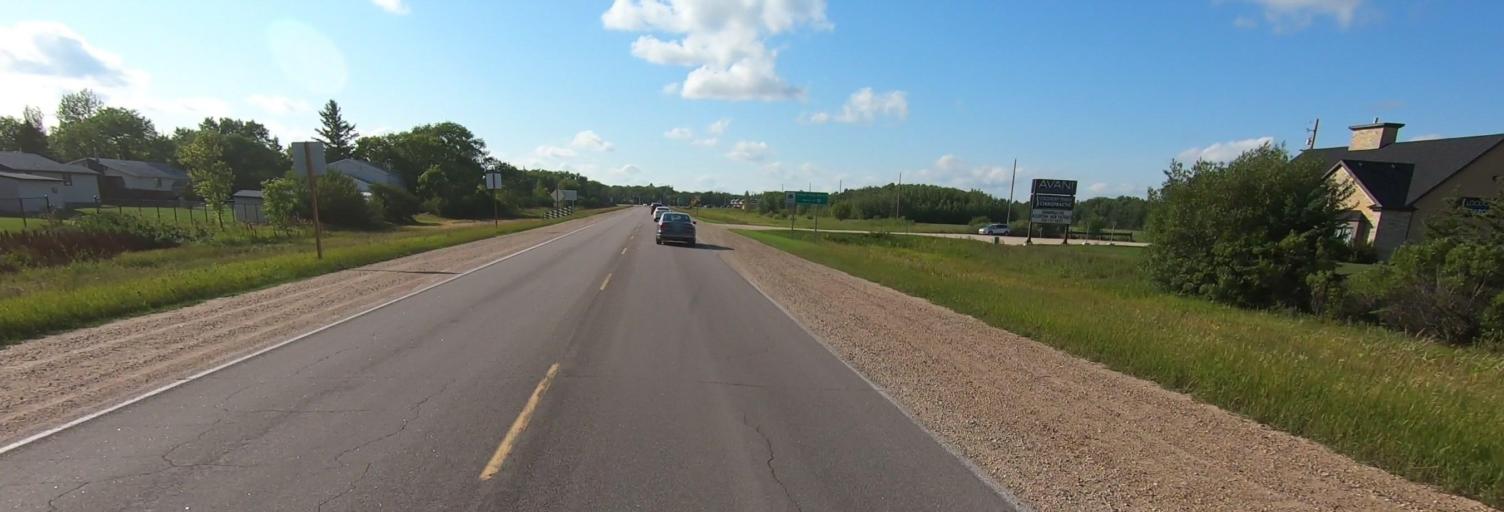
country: CA
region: Manitoba
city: Selkirk
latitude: 50.0859
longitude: -96.9488
